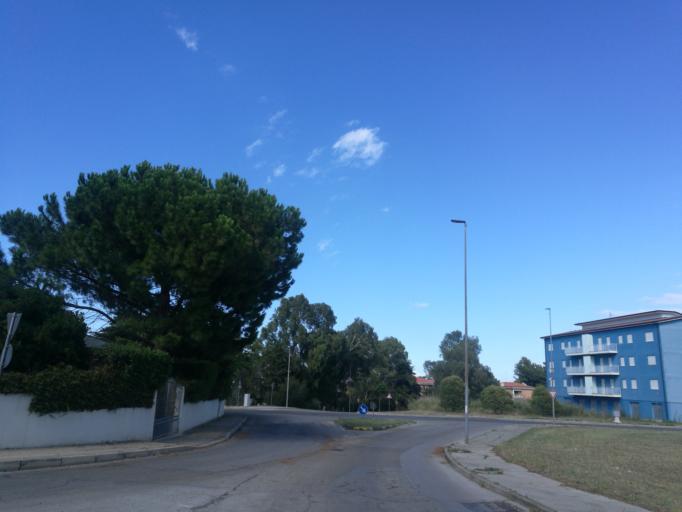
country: IT
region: Molise
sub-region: Provincia di Campobasso
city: Termoli
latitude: 41.9820
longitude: 14.9832
